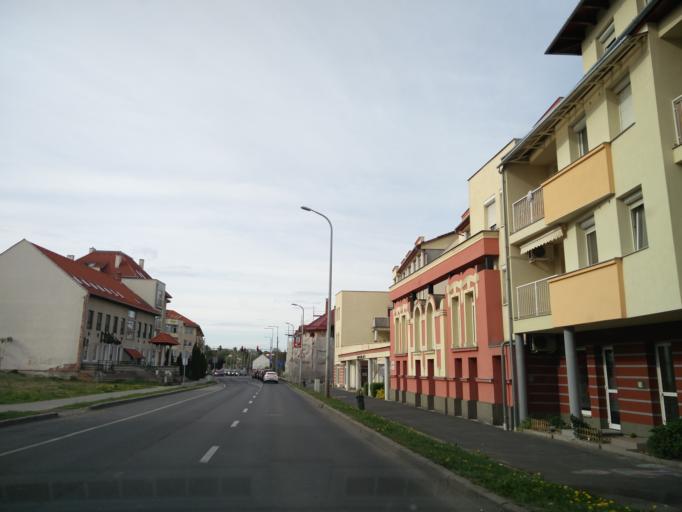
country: HU
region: Zala
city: Zalaegerszeg
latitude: 46.8465
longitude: 16.8467
